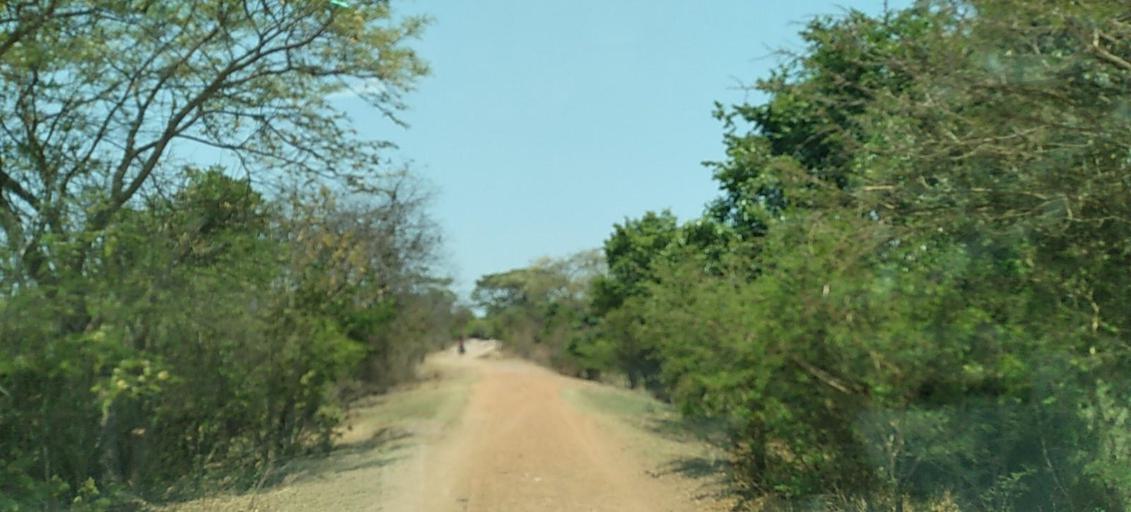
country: ZM
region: Copperbelt
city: Mpongwe
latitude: -13.8671
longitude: 27.8837
